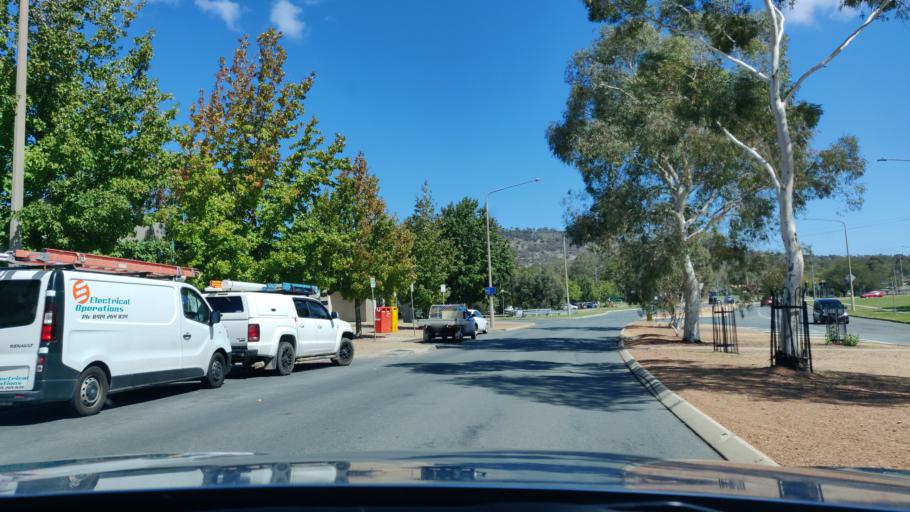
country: AU
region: Australian Capital Territory
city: Macarthur
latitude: -35.3643
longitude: 149.0945
